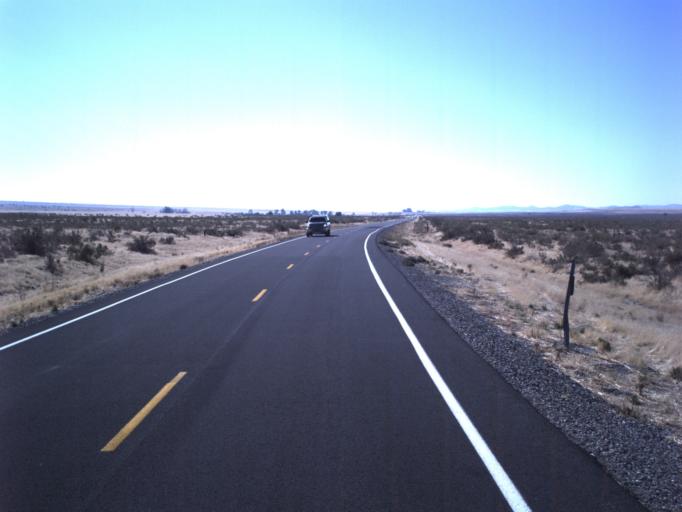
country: US
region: Utah
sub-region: Tooele County
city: Grantsville
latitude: 40.4825
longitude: -112.7455
